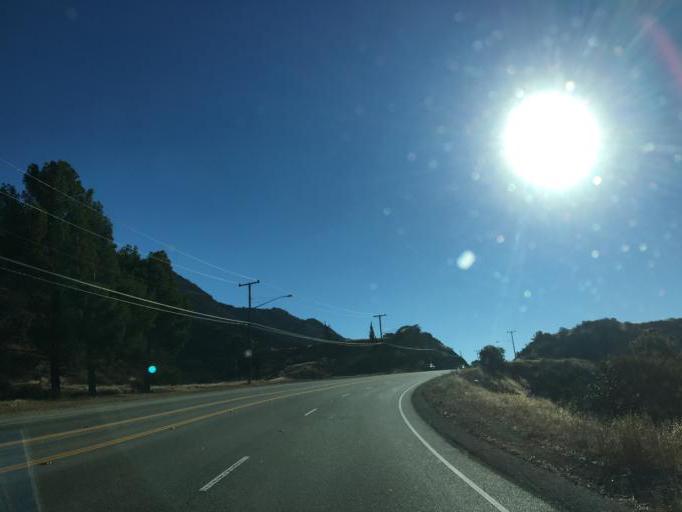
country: US
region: California
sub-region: Los Angeles County
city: Agoura Hills
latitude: 34.1295
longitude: -118.7752
